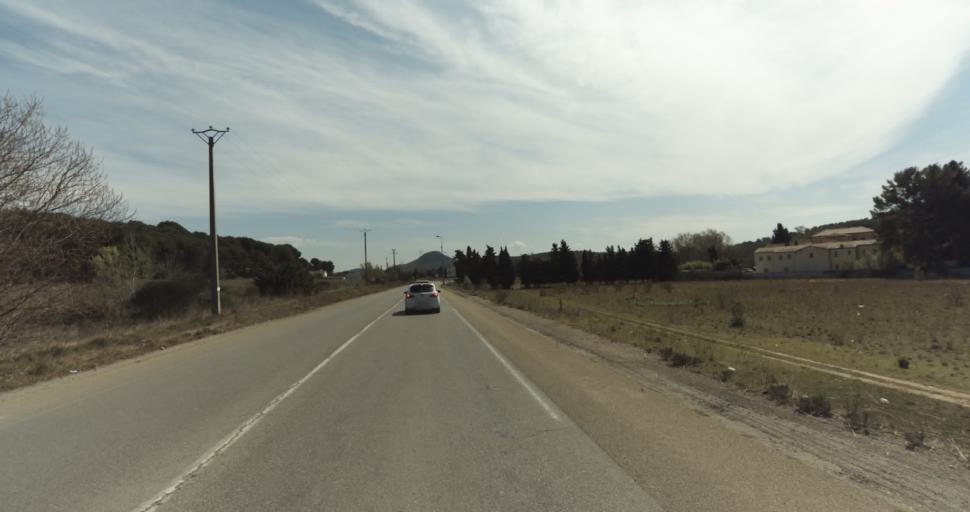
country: FR
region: Provence-Alpes-Cote d'Azur
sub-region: Departement des Bouches-du-Rhone
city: Coudoux
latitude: 43.5446
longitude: 5.2575
